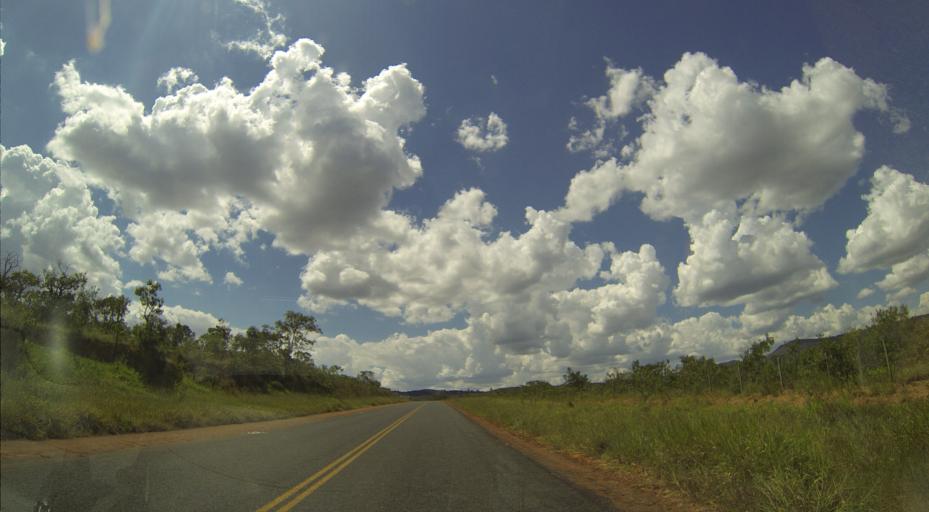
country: BR
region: Minas Gerais
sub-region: Serro
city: Serro
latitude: -18.4869
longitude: -43.4842
